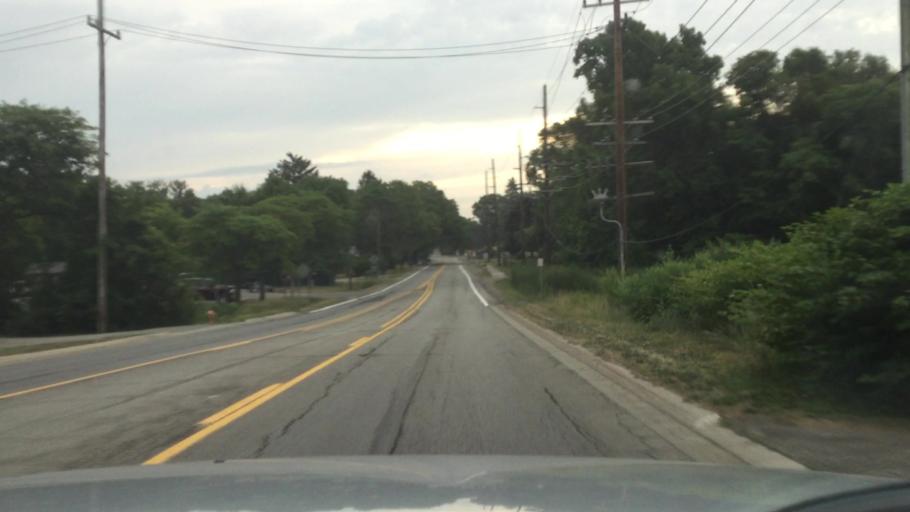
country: US
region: Michigan
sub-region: Oakland County
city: Waterford
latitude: 42.6812
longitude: -83.4307
